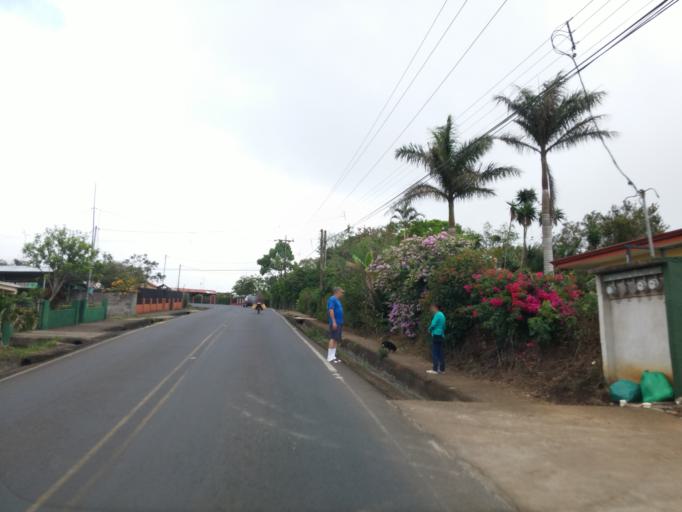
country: CR
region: Alajuela
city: San Ramon
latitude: 10.1261
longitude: -84.4717
